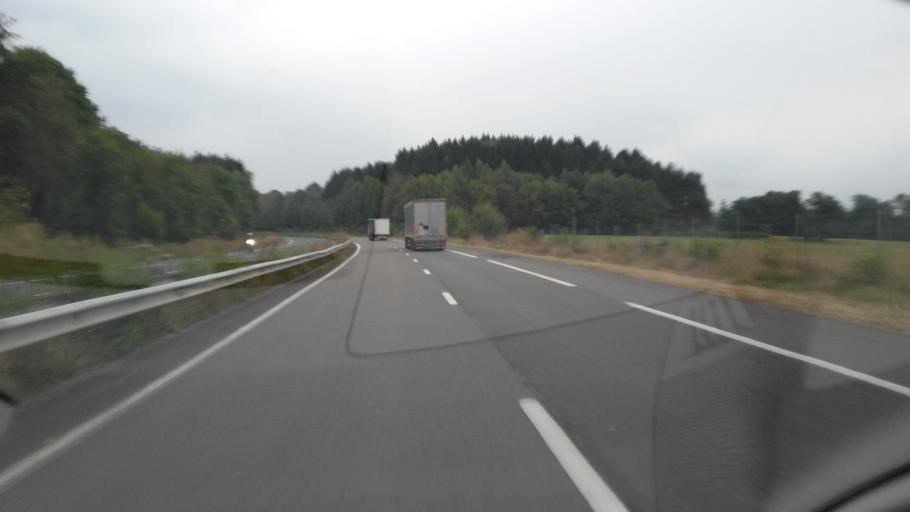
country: FR
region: Champagne-Ardenne
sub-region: Departement des Ardennes
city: Douzy
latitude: 49.7150
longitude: 5.0134
